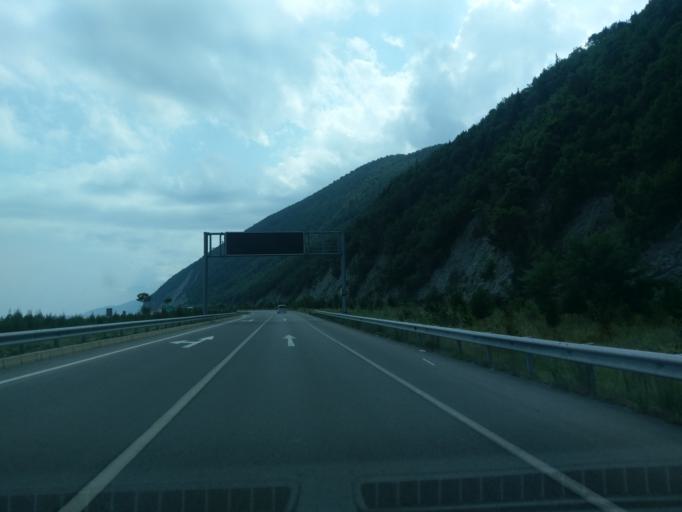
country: TR
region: Sinop
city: Gerze
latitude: 41.7494
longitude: 35.2406
